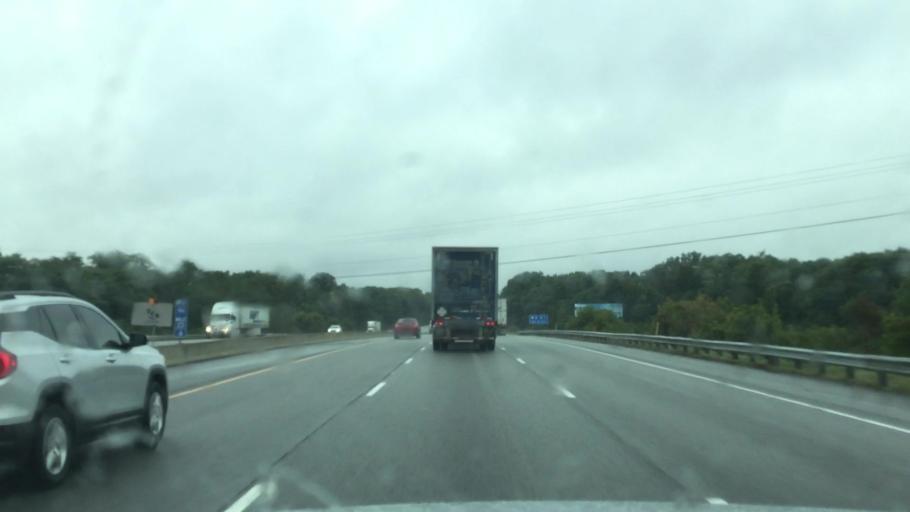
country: US
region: Indiana
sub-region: Porter County
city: Porter
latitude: 41.6141
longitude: -87.0863
